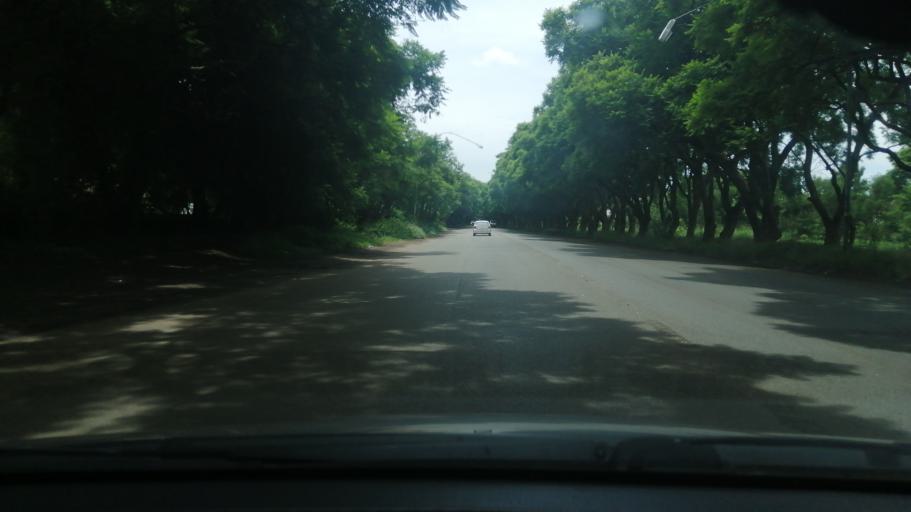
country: ZW
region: Harare
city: Harare
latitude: -17.8082
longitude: 31.0403
